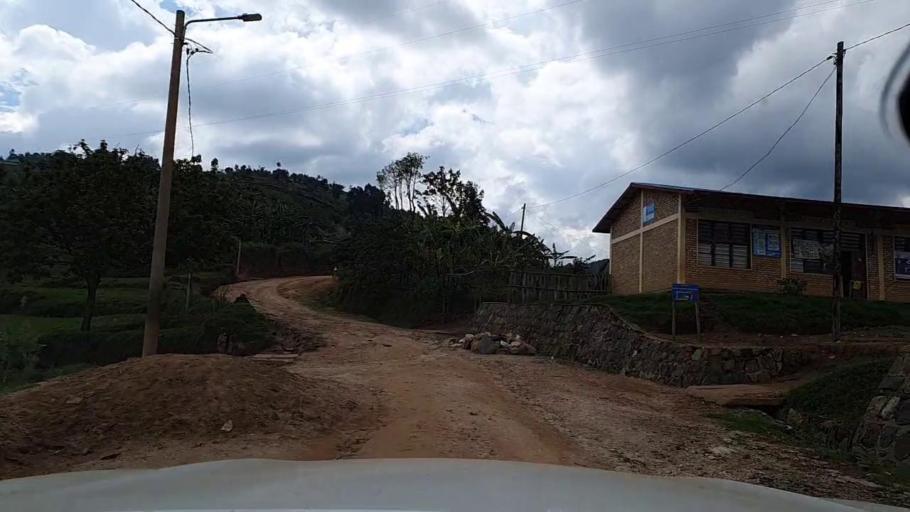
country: RW
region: Southern Province
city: Nzega
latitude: -2.7040
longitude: 29.4327
